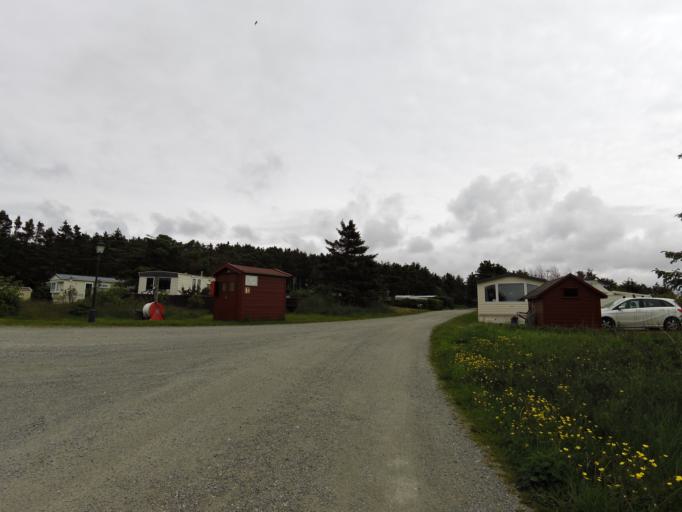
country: NO
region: Rogaland
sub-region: Ha
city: Naerbo
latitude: 58.6946
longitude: 5.5514
